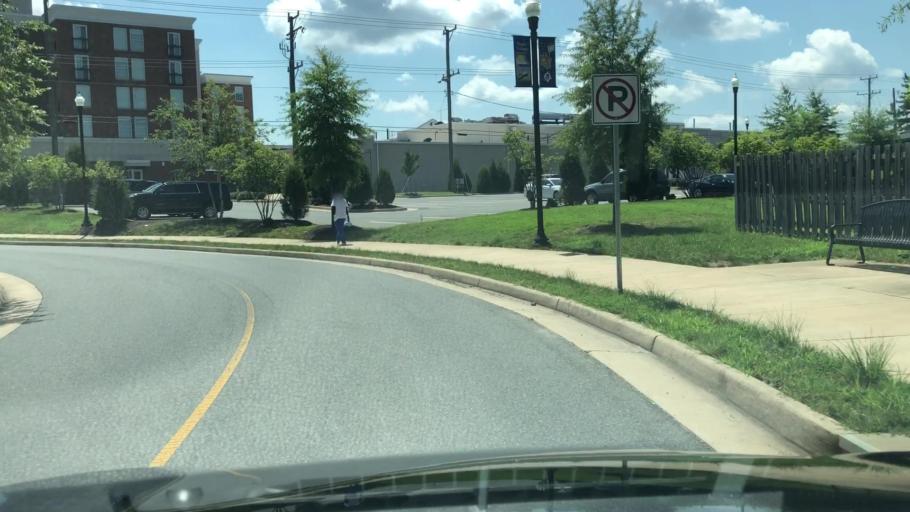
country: US
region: Virginia
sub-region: Stafford County
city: Falmouth
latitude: 38.3079
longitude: -77.4824
